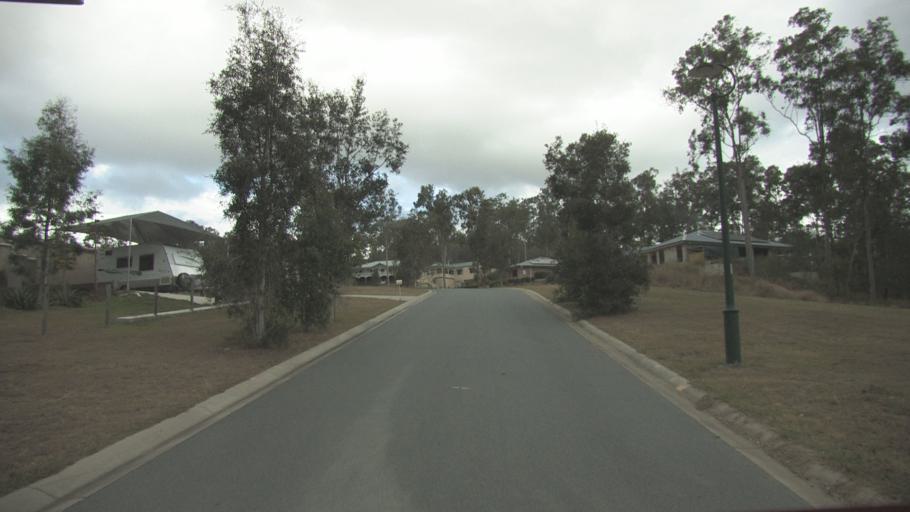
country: AU
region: Queensland
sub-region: Logan
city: Cedar Vale
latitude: -27.8649
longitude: 153.0739
